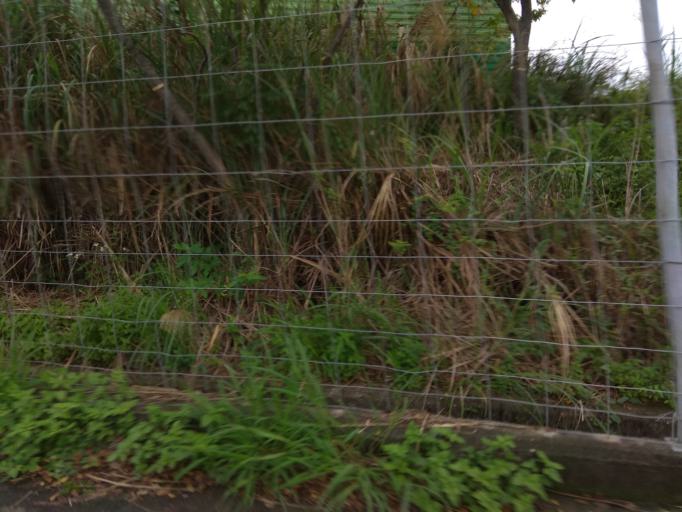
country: TW
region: Taiwan
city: Taoyuan City
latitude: 25.0518
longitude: 121.2159
